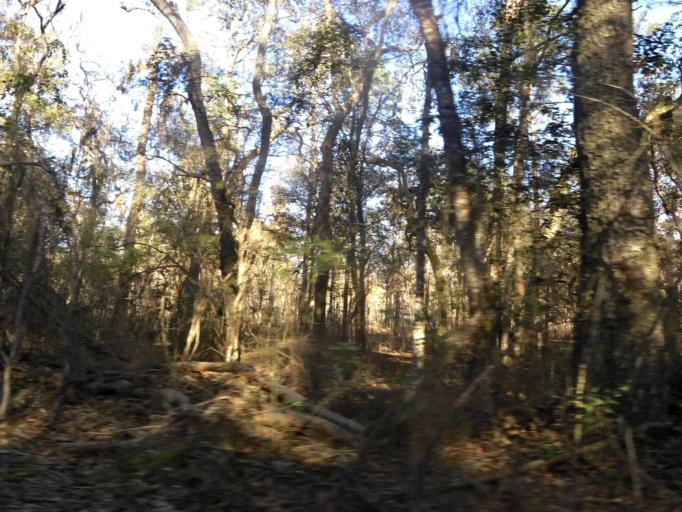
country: US
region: Florida
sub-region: Clay County
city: Middleburg
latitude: 30.1390
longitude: -81.9057
